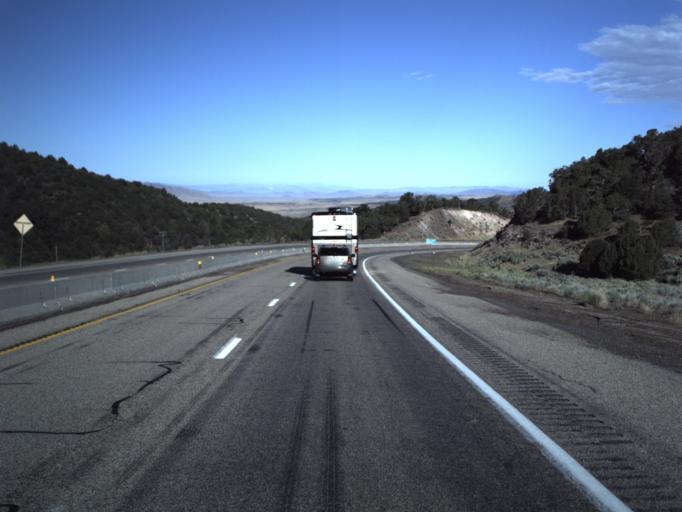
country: US
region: Utah
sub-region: Beaver County
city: Beaver
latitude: 38.5938
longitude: -112.5040
